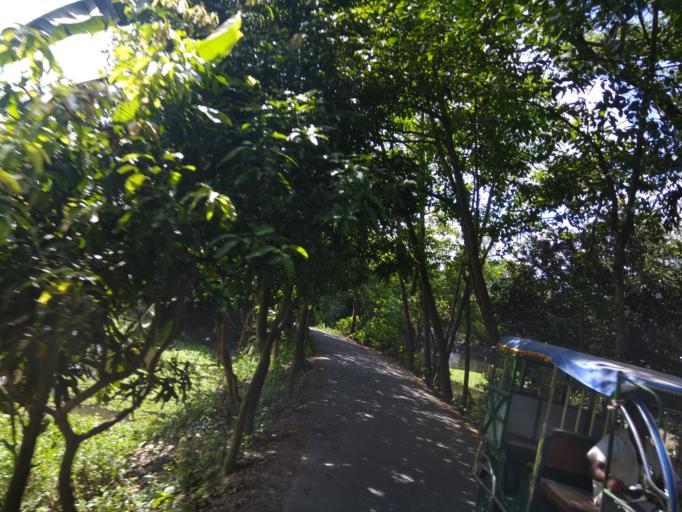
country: BD
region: Dhaka
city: Narayanganj
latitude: 23.4429
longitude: 90.4603
